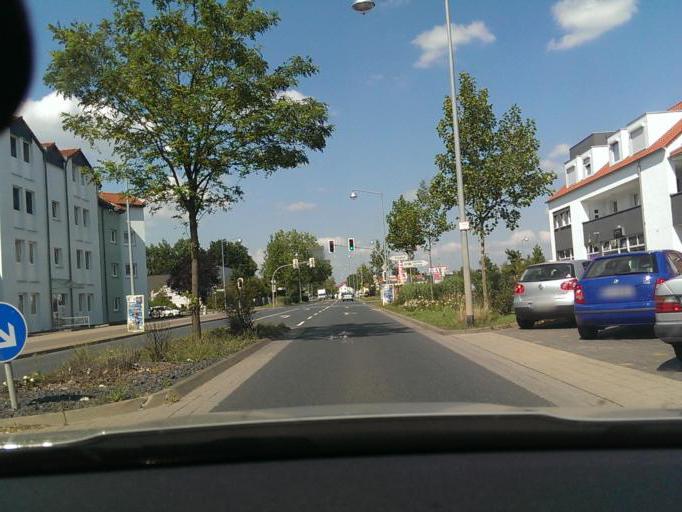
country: DE
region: Lower Saxony
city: Langenhagen
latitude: 52.4777
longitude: 9.7341
